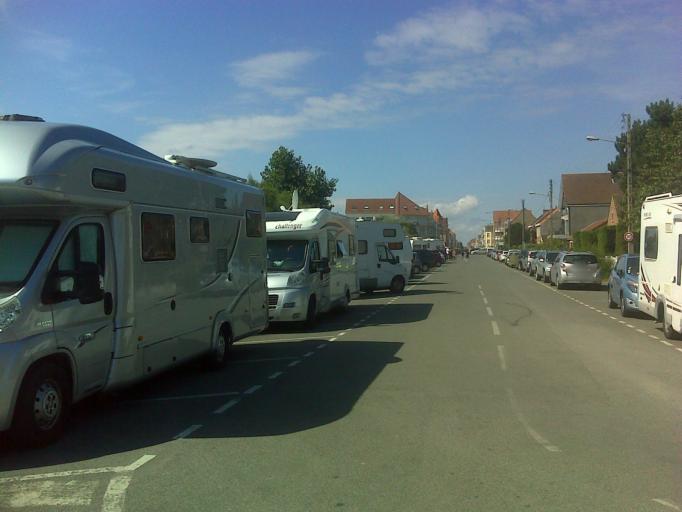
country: FR
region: Nord-Pas-de-Calais
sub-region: Departement du Nord
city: Bray-Dunes
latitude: 51.0807
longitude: 2.5235
